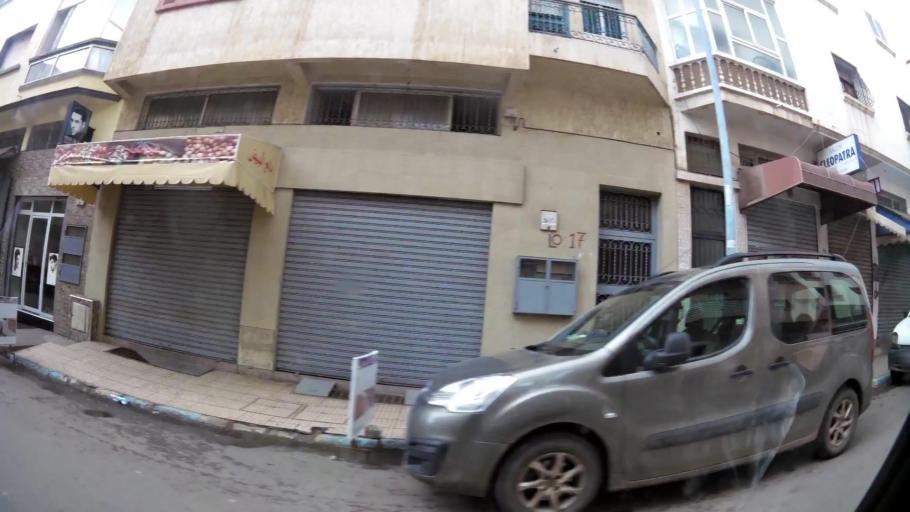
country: MA
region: Grand Casablanca
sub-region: Casablanca
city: Casablanca
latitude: 33.5426
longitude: -7.6816
